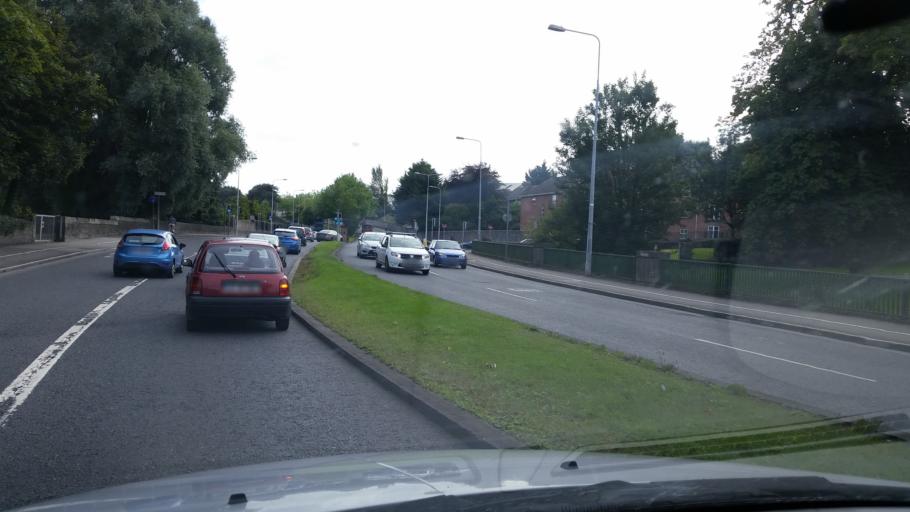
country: IE
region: Leinster
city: Cabra
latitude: 53.3766
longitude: -6.2868
